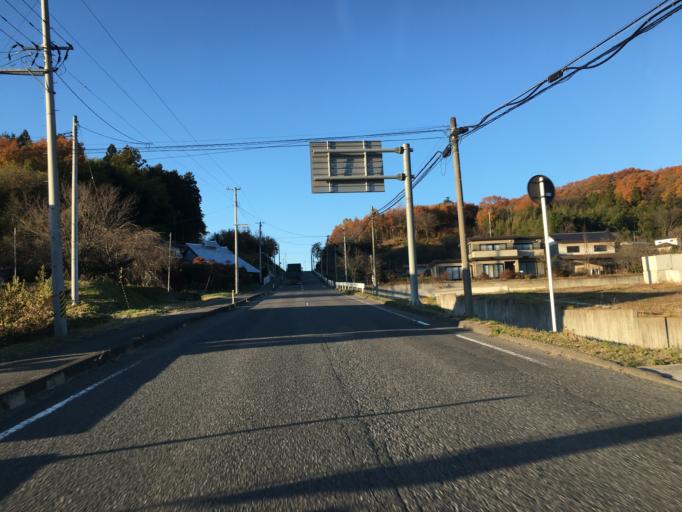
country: JP
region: Fukushima
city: Miharu
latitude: 37.4445
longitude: 140.4444
